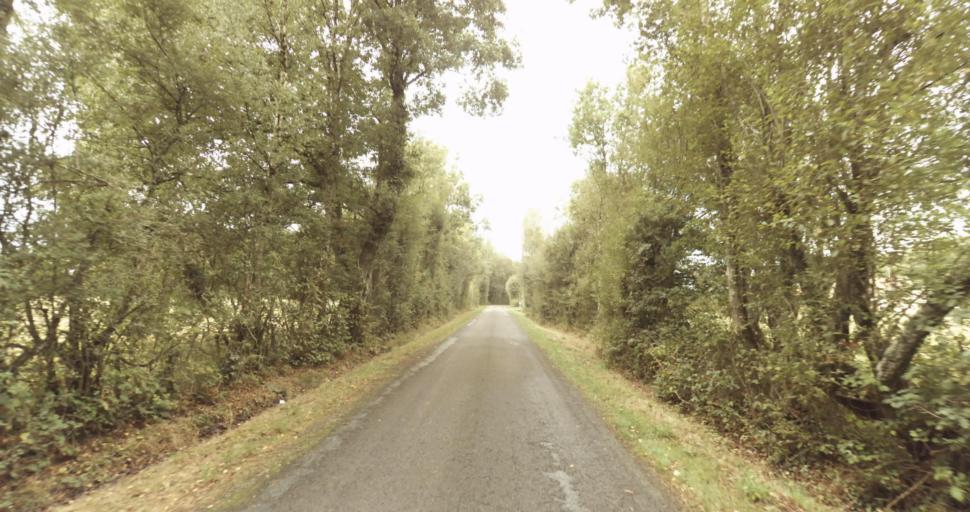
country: FR
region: Lower Normandy
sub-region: Departement de l'Orne
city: Sainte-Gauburge-Sainte-Colombe
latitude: 48.6977
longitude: 0.4558
